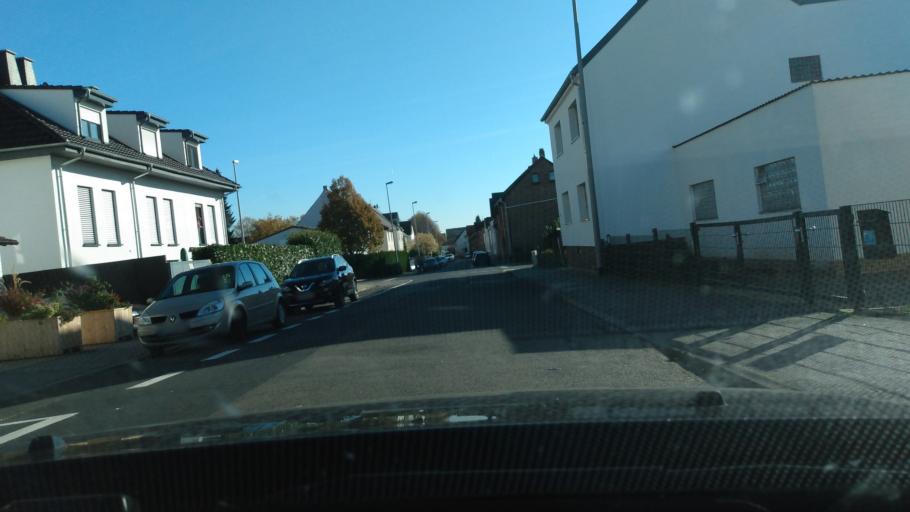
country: DE
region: Hesse
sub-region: Regierungsbezirk Darmstadt
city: Kriftel
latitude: 50.0858
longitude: 8.4644
